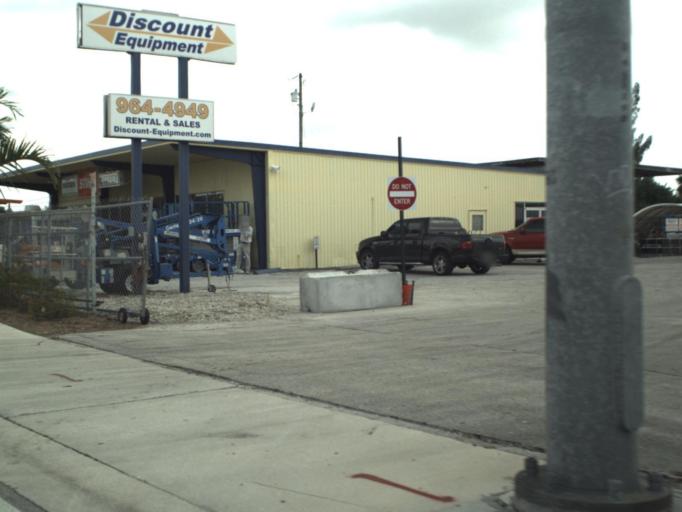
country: US
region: Florida
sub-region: Palm Beach County
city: Lake Clarke Shores
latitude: 26.6614
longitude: -80.0882
